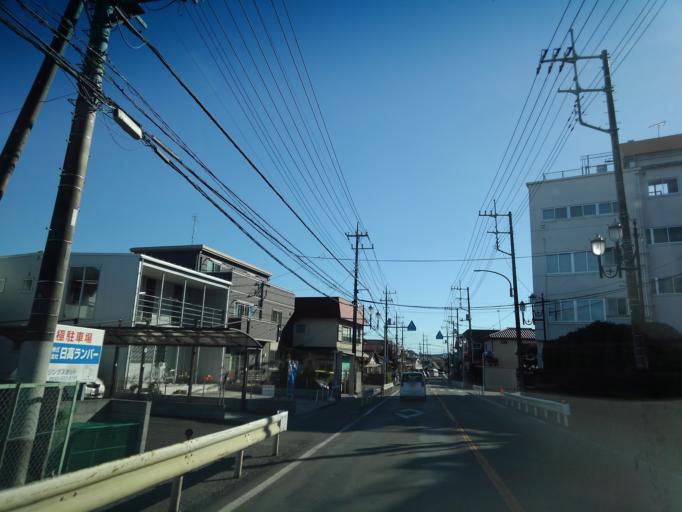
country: JP
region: Saitama
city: Hanno
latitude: 35.8490
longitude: 139.3193
